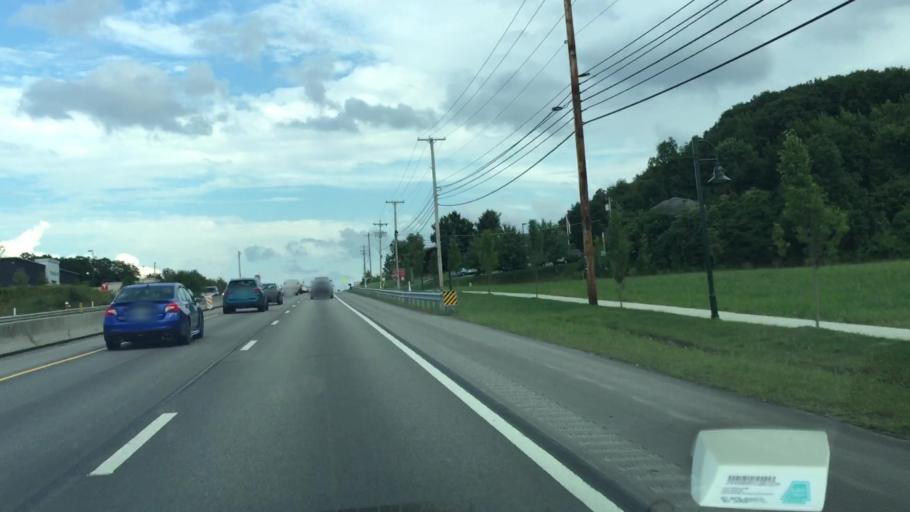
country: US
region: Pennsylvania
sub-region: Allegheny County
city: Bradford Woods
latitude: 40.6467
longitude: -80.0733
